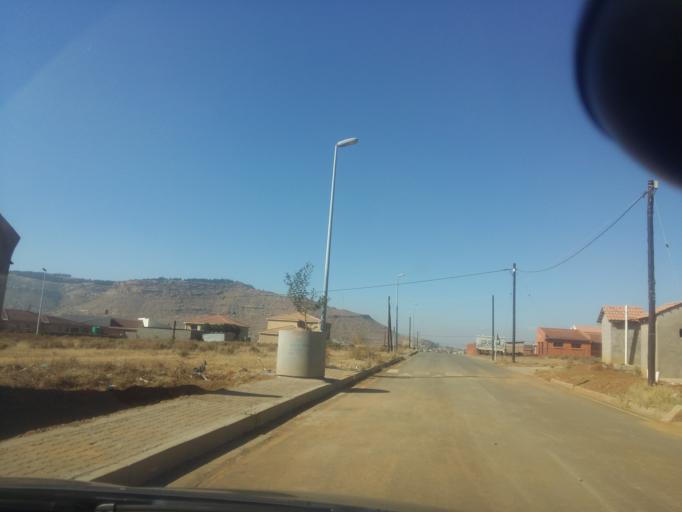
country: LS
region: Maseru
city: Maseru
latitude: -29.3436
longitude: 27.4462
